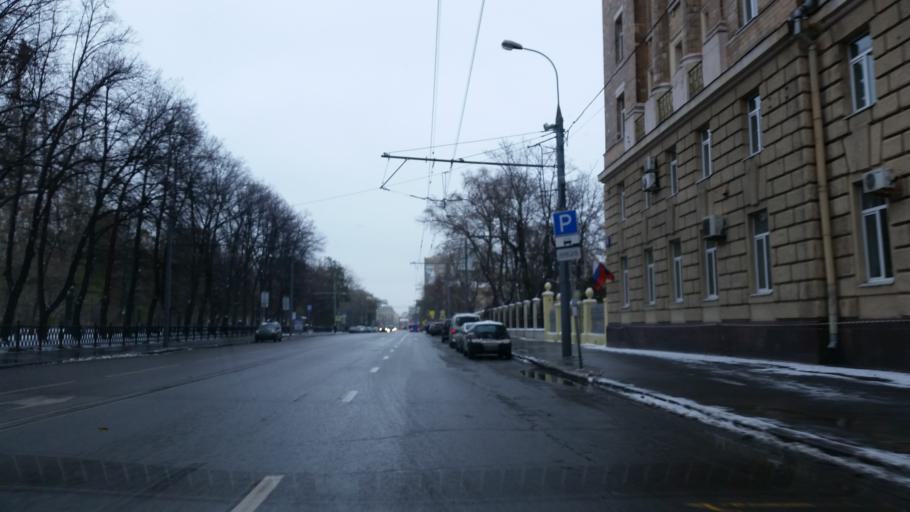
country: RU
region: Moskovskaya
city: Dorogomilovo
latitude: 55.7339
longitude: 37.5759
